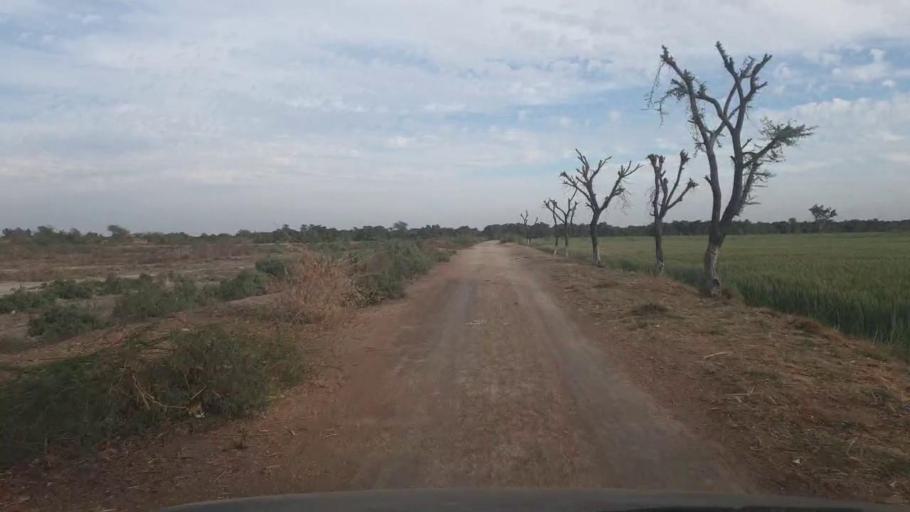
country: PK
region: Sindh
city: Samaro
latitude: 25.3282
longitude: 69.2646
